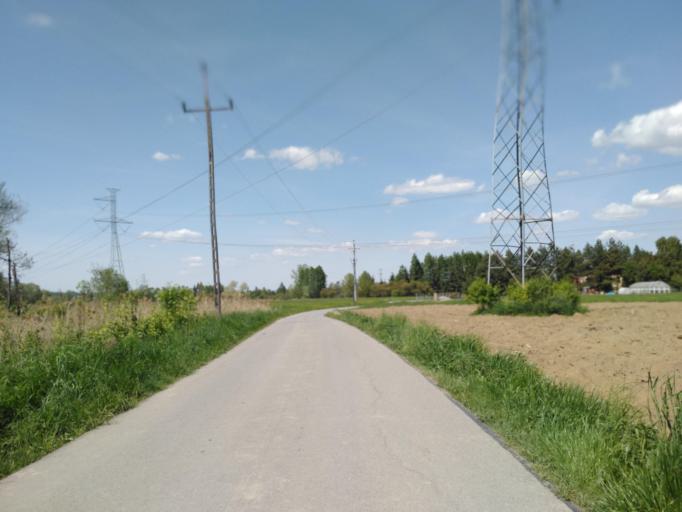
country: PL
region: Subcarpathian Voivodeship
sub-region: Powiat krosnienski
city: Odrzykon
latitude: 49.7275
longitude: 21.7305
